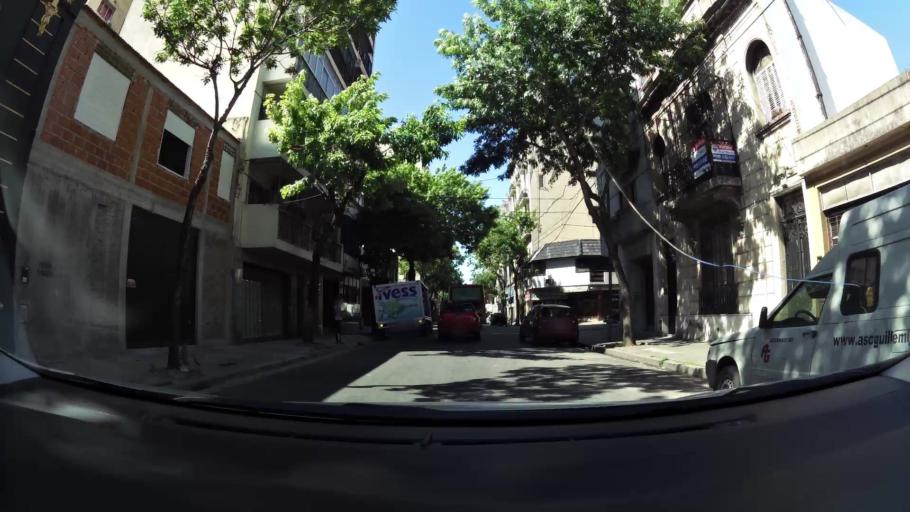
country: AR
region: Buenos Aires F.D.
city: Buenos Aires
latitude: -34.6232
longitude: -58.3844
